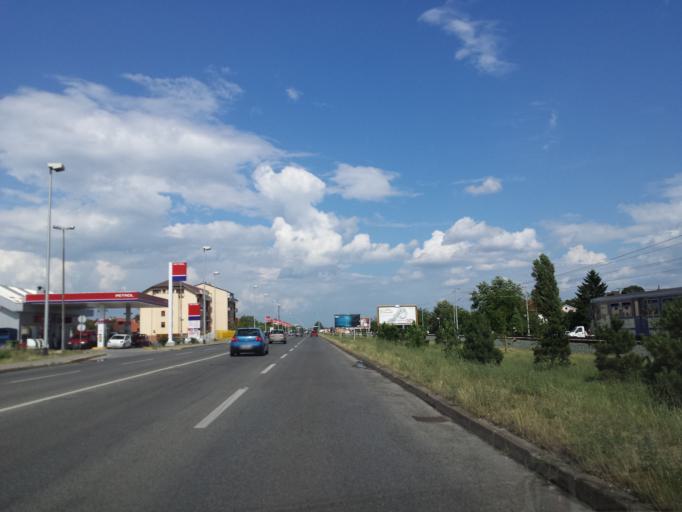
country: HR
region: Grad Zagreb
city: Dubrava
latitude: 45.8200
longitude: 16.0572
